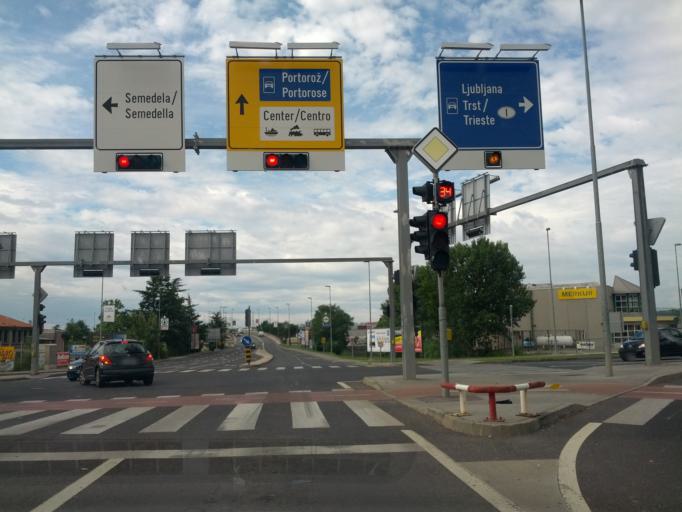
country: SI
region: Koper-Capodistria
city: Koper
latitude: 45.5341
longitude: 13.7352
